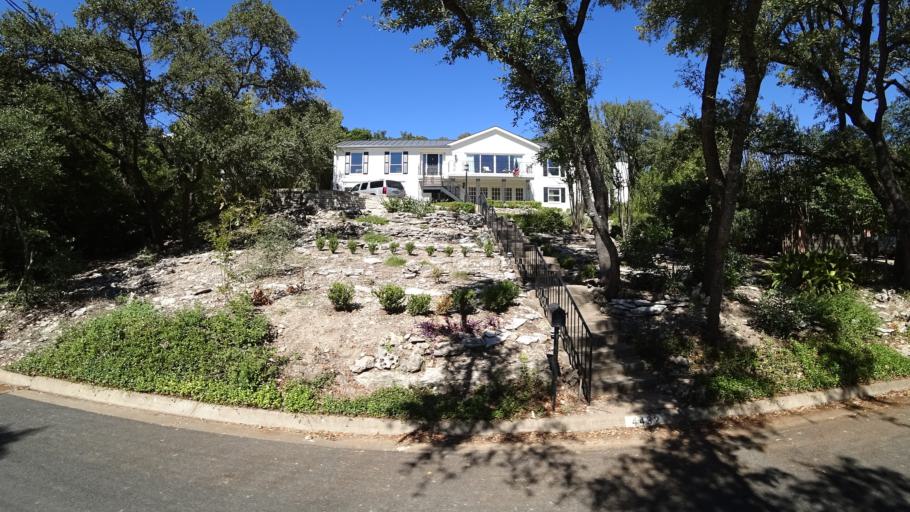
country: US
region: Texas
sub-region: Travis County
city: West Lake Hills
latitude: 30.3279
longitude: -97.7712
